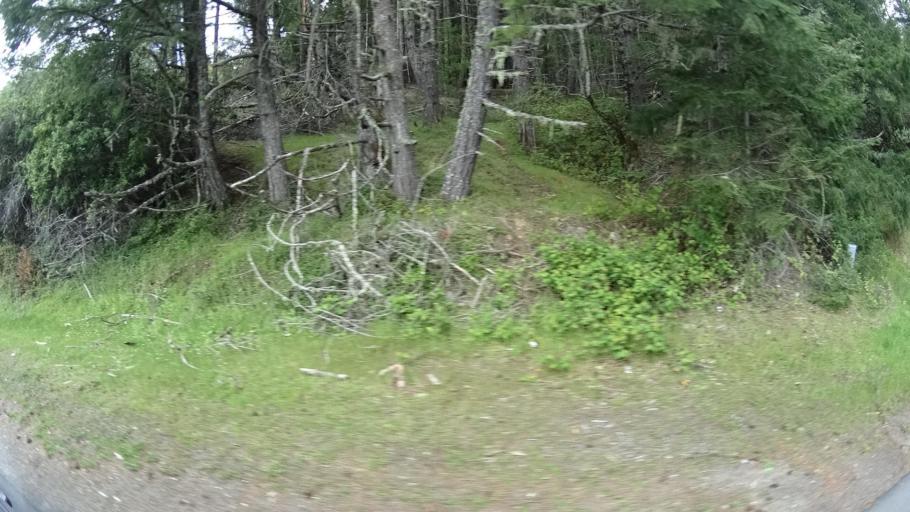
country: US
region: California
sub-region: Humboldt County
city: Redway
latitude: 40.1300
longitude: -123.6327
